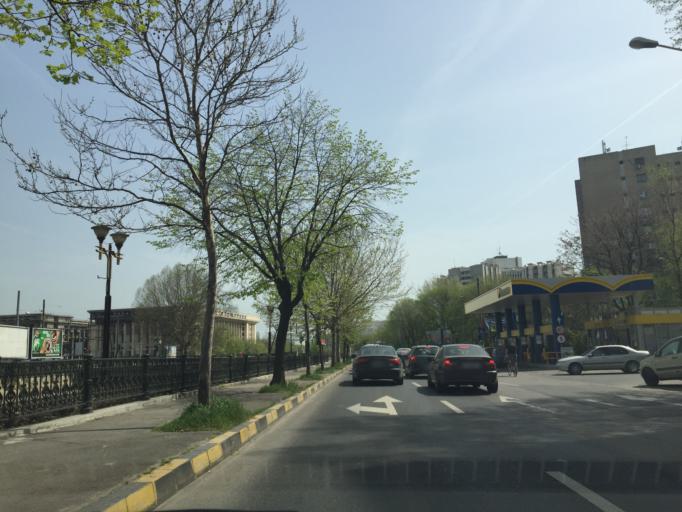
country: RO
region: Bucuresti
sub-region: Municipiul Bucuresti
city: Bucuresti
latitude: 44.4387
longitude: 26.0690
